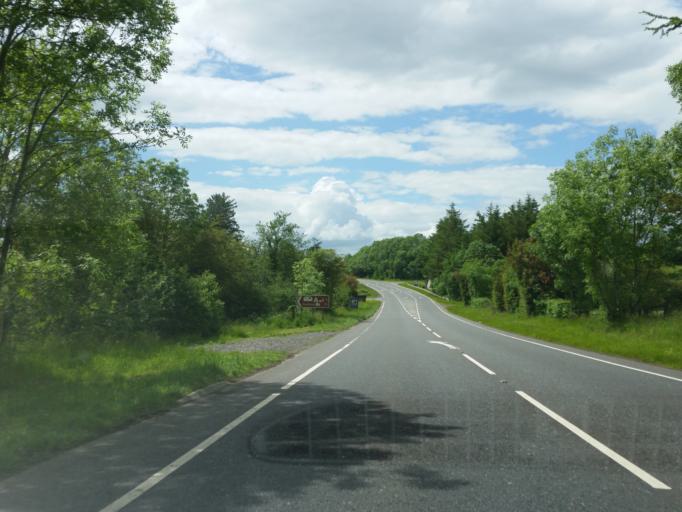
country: GB
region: Northern Ireland
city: Fivemiletown
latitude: 54.4022
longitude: -7.2021
